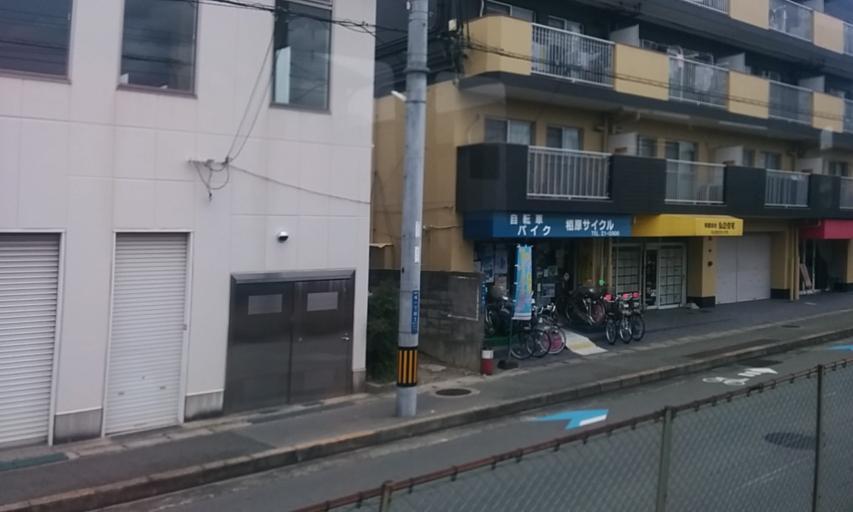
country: JP
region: Osaka
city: Mino
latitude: 34.8258
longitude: 135.4663
